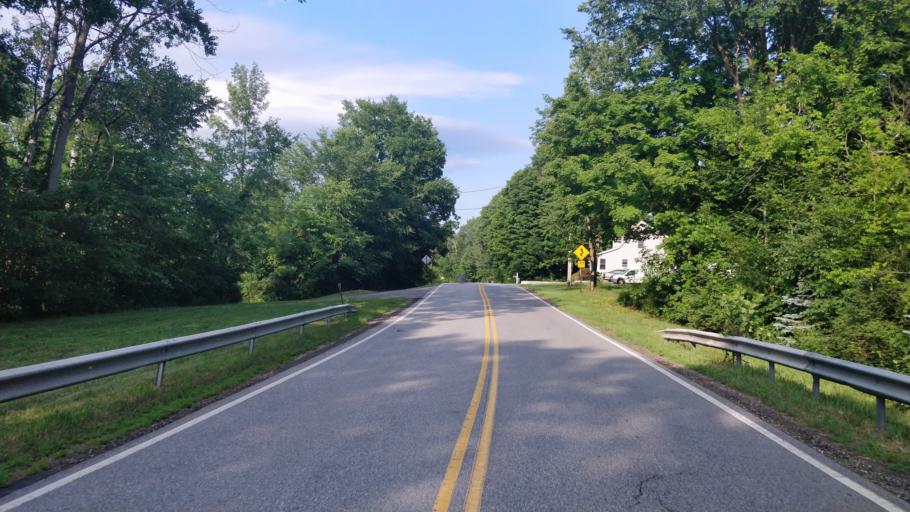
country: US
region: New York
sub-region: Saratoga County
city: North Ballston Spa
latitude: 43.0242
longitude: -73.8010
